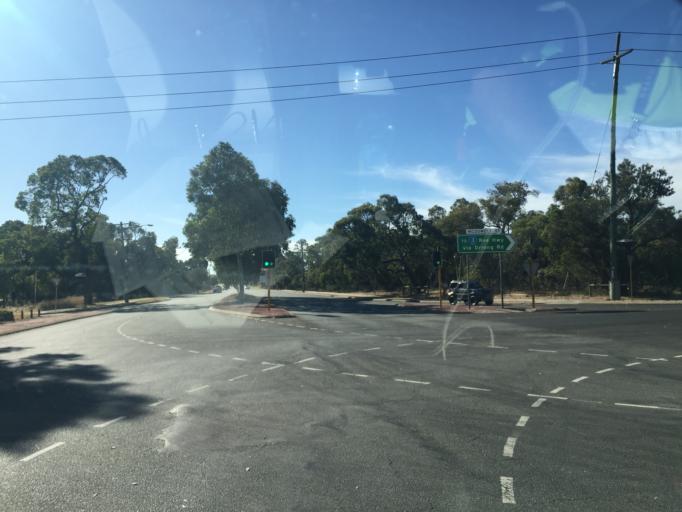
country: AU
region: Western Australia
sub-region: Canning
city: East Cannington
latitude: -31.9999
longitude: 115.9624
